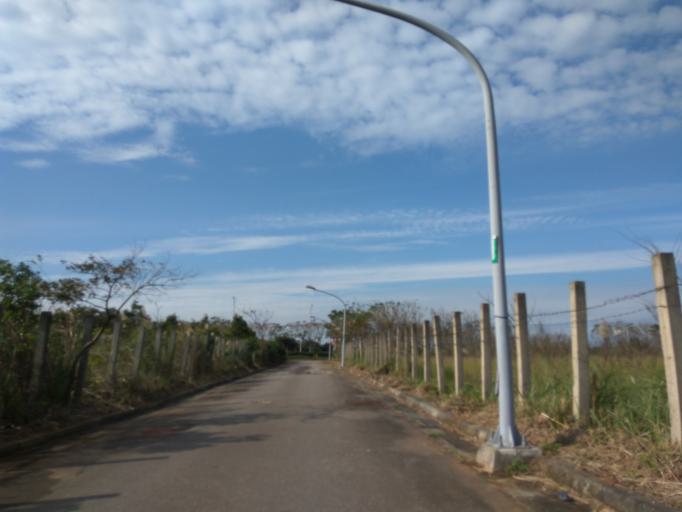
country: TW
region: Taiwan
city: Taoyuan City
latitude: 25.0521
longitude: 121.1759
